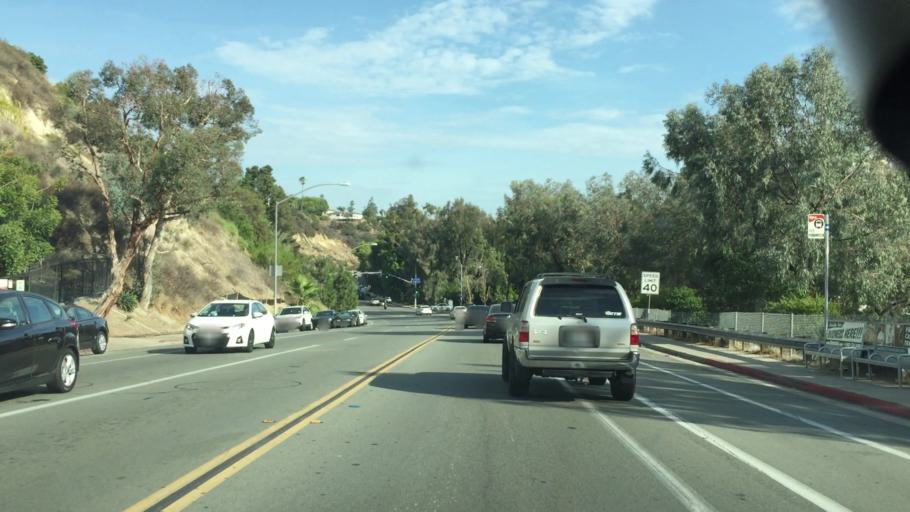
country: US
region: California
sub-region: San Diego County
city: Lemon Grove
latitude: 32.7695
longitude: -117.0858
